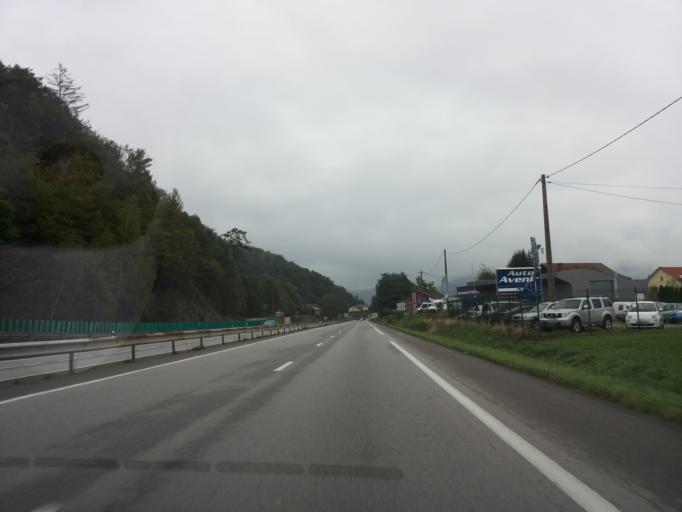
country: FR
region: Lorraine
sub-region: Departement des Vosges
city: Saint-Nabord
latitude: 48.0583
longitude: 6.5915
